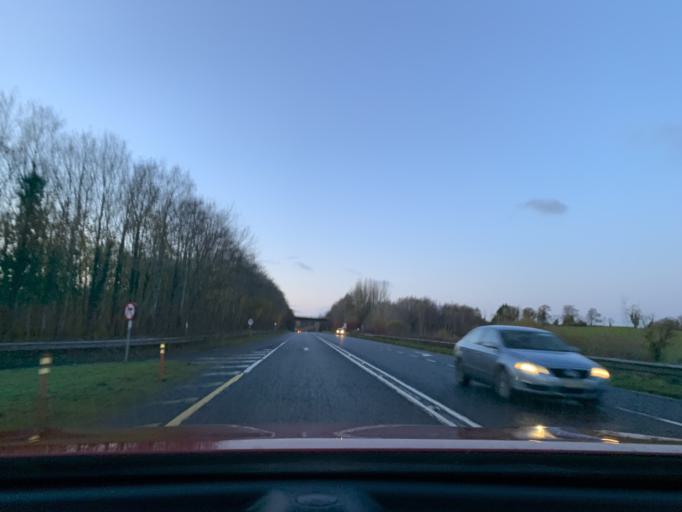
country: IE
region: Connaught
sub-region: County Leitrim
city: Carrick-on-Shannon
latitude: 53.9287
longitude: -8.0003
